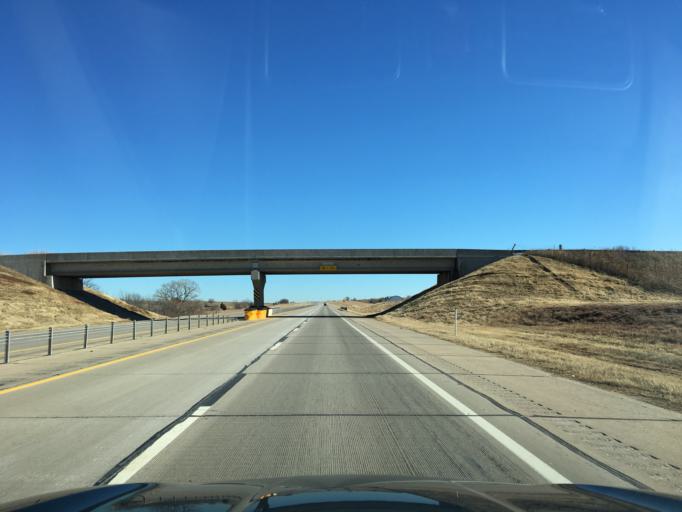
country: US
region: Oklahoma
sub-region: Noble County
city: Perry
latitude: 36.3928
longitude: -97.1943
